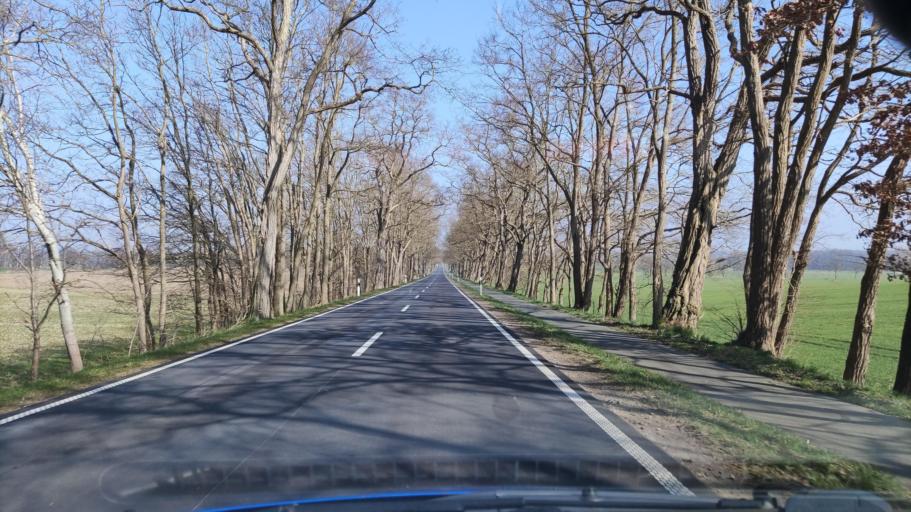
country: DE
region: Lower Saxony
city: Clenze
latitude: 52.9466
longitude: 10.9662
